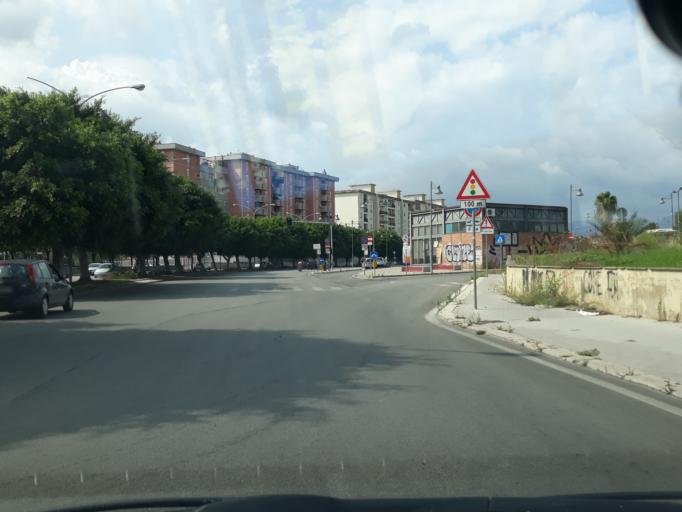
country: IT
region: Sicily
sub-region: Palermo
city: Palermo
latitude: 38.0986
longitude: 13.3462
